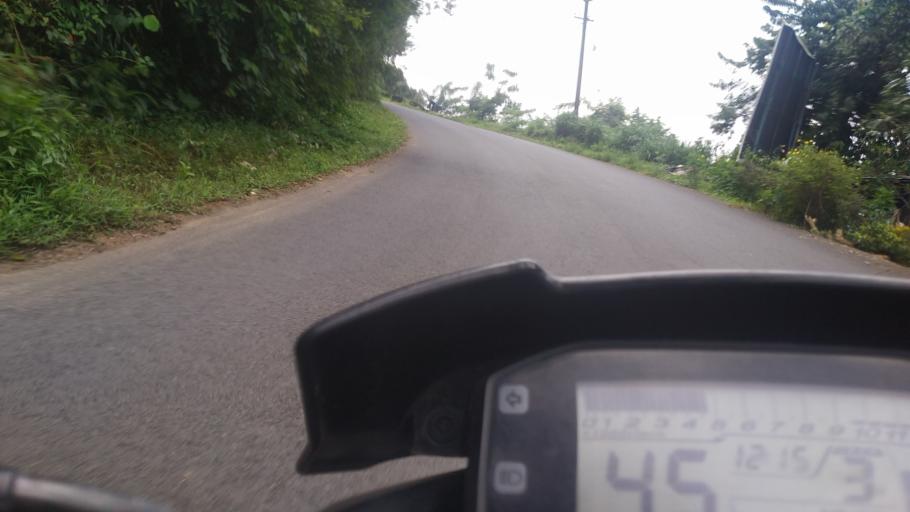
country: IN
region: Kerala
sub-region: Idukki
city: Munnar
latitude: 10.0127
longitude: 77.0074
